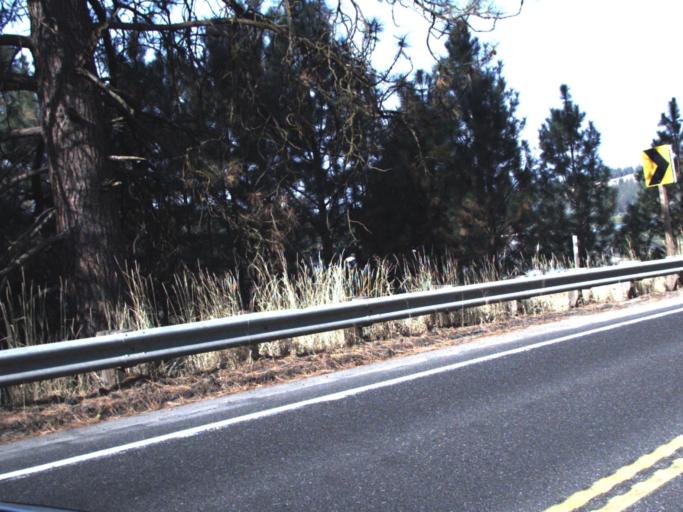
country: US
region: Washington
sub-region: Spokane County
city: Fairwood
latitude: 47.7988
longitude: -117.5386
